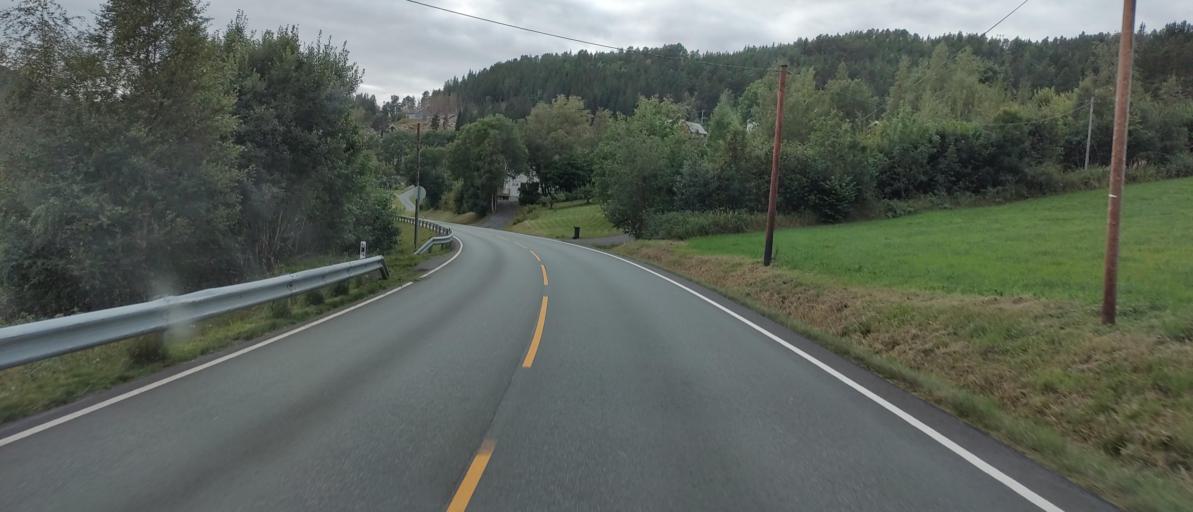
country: NO
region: More og Romsdal
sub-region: Rauma
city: Andalsnes
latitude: 62.5802
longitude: 7.5613
